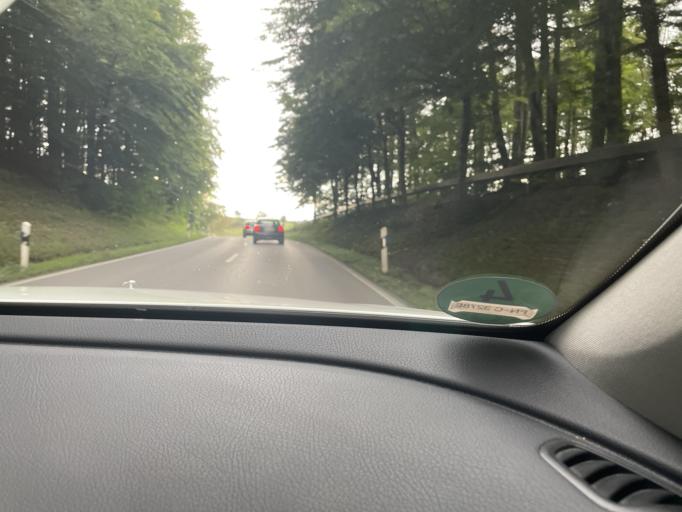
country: DE
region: Baden-Wuerttemberg
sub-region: Tuebingen Region
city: Markdorf
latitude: 47.7039
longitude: 9.4193
